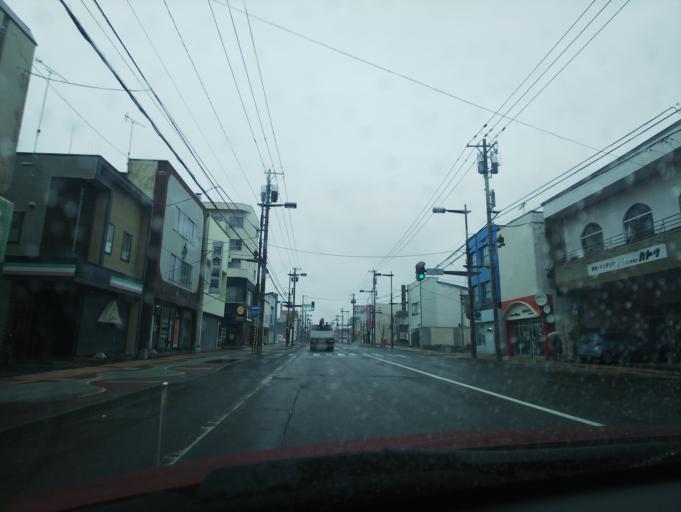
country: JP
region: Hokkaido
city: Nayoro
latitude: 44.1769
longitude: 142.3920
